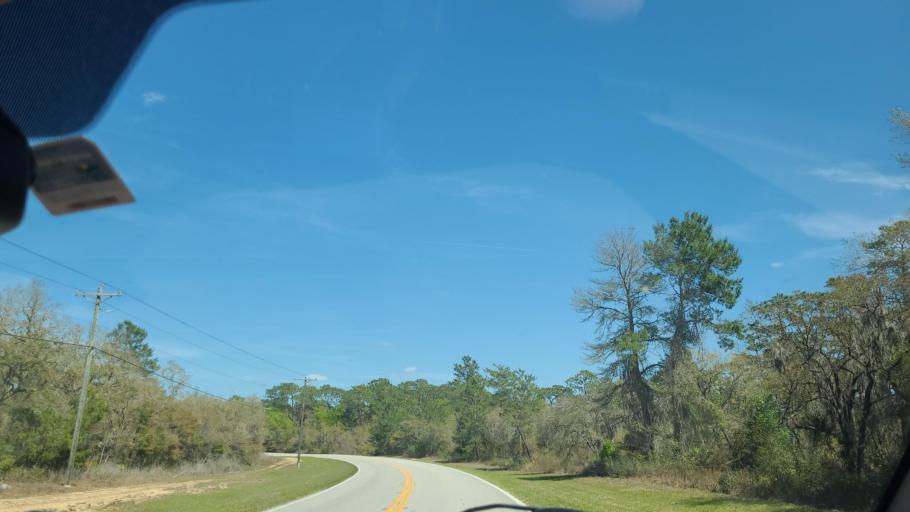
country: US
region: Florida
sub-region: Putnam County
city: Interlachen
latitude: 29.3662
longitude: -81.8099
